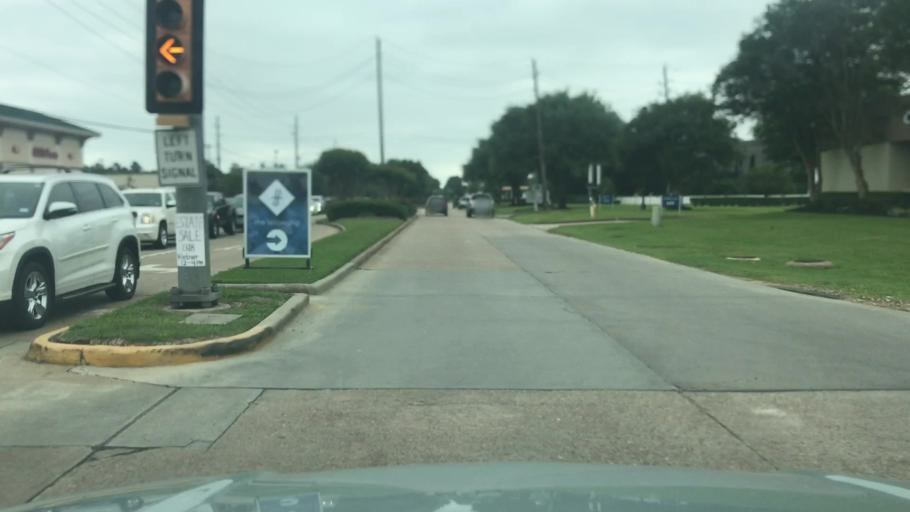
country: US
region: Texas
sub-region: Harris County
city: Katy
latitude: 29.7731
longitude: -95.8184
